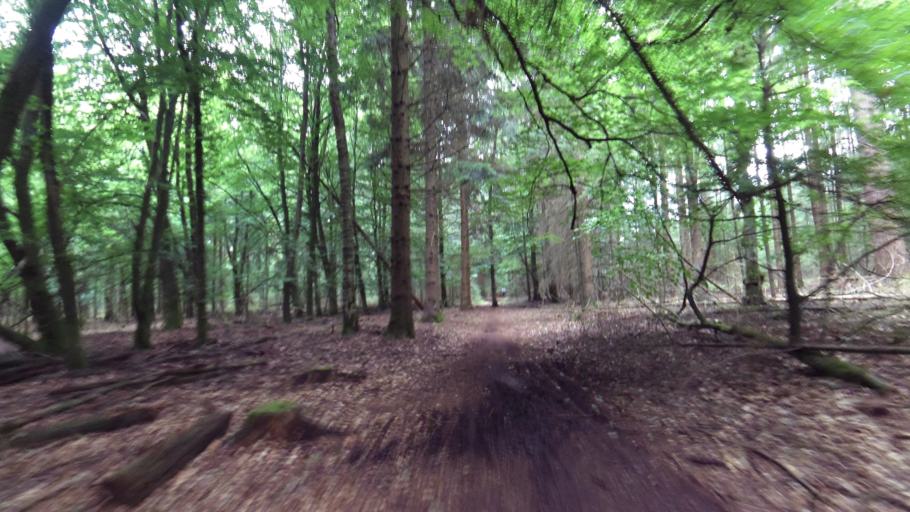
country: NL
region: Gelderland
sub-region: Gemeente Apeldoorn
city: Apeldoorn
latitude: 52.2062
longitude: 5.8951
